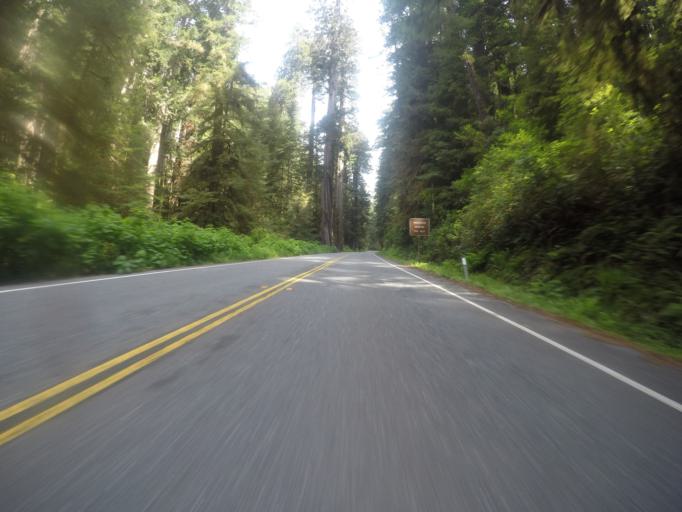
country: US
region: California
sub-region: Del Norte County
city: Bertsch-Oceanview
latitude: 41.4363
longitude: -124.0399
